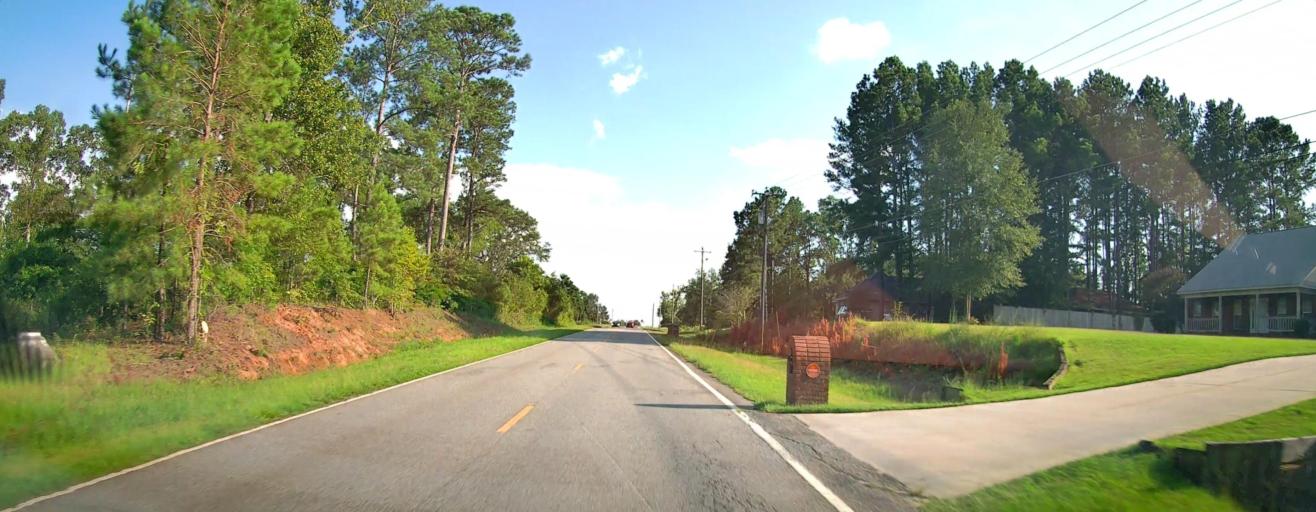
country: US
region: Georgia
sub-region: Houston County
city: Robins Air Force Base
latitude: 32.5549
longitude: -83.6045
